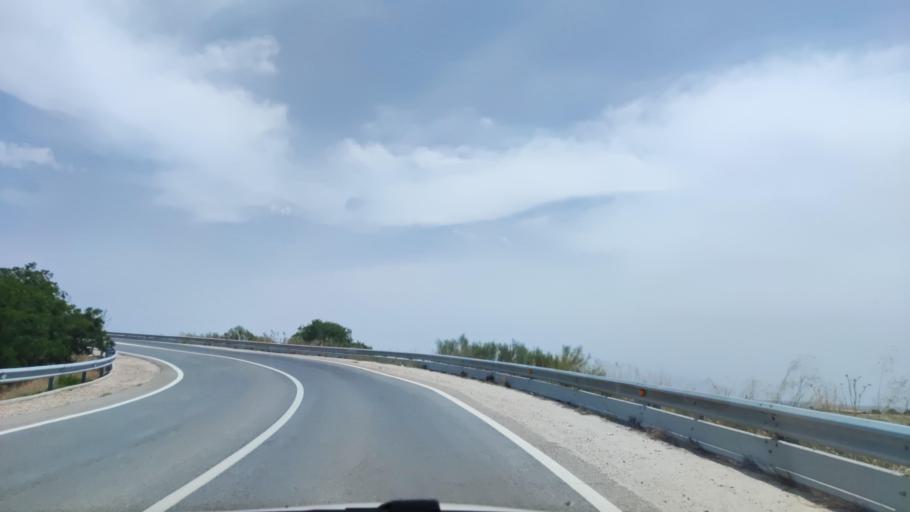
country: ES
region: Madrid
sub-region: Provincia de Madrid
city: Navalcarnero
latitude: 40.2783
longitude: -4.0235
